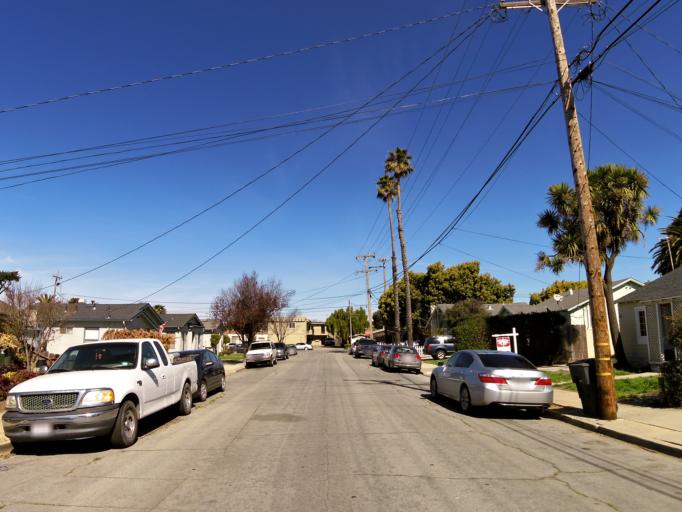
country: US
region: California
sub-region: Monterey County
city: Salinas
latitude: 36.6751
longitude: -121.6639
